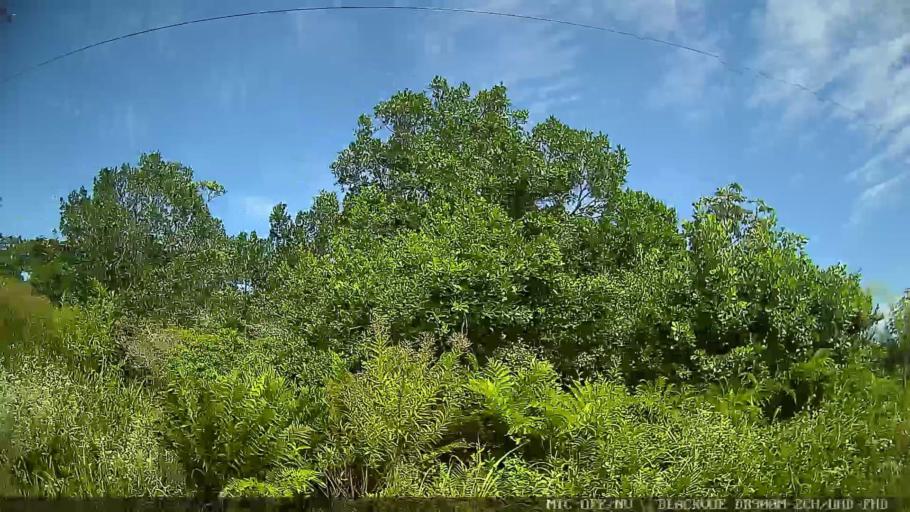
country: BR
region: Sao Paulo
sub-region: Iguape
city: Iguape
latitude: -24.7758
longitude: -47.6095
